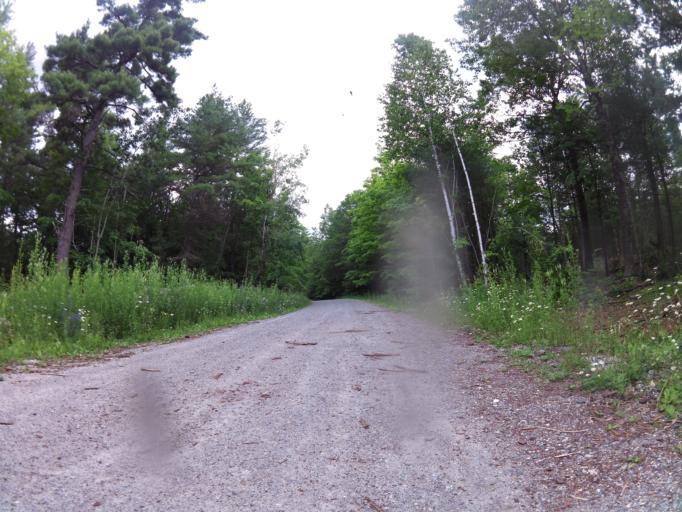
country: CA
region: Ontario
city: Perth
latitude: 45.0091
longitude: -76.5881
